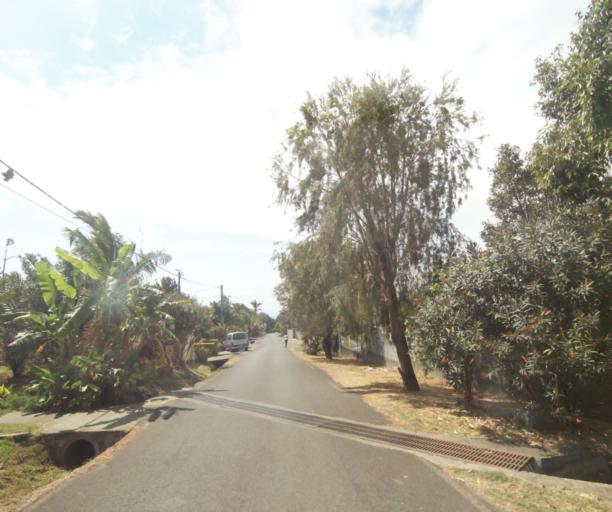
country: RE
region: Reunion
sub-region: Reunion
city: Saint-Paul
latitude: -21.0561
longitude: 55.2588
